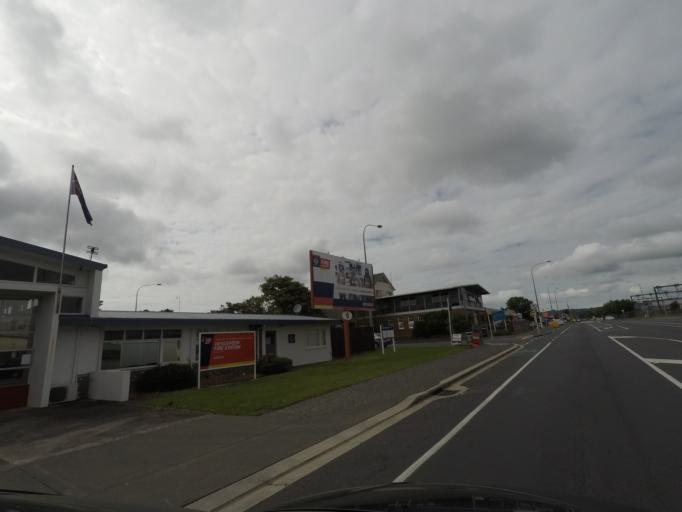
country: NZ
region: Auckland
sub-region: Auckland
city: Rosebank
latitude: -36.8843
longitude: 174.6315
